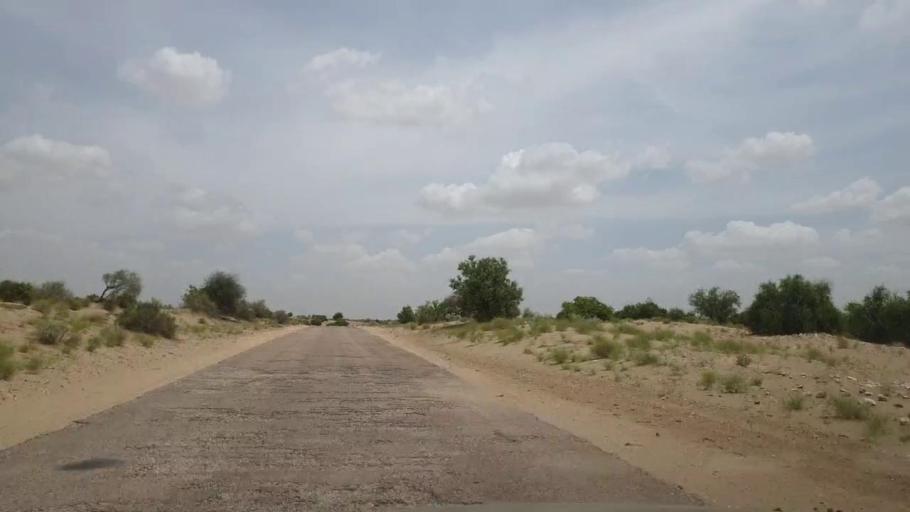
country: PK
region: Sindh
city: Kot Diji
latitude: 27.1889
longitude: 69.1691
